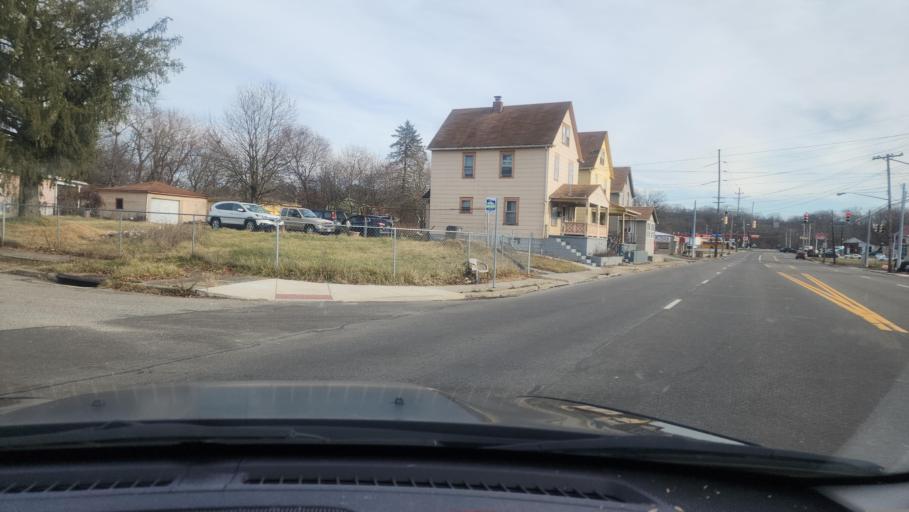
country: US
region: Ohio
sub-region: Mahoning County
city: Campbell
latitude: 41.0968
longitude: -80.6190
